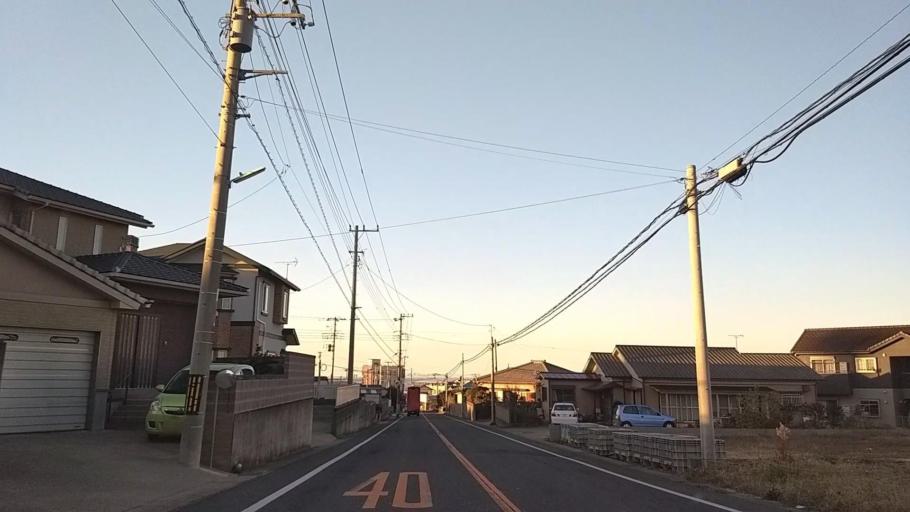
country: JP
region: Chiba
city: Hasaki
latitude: 35.7402
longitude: 140.8591
